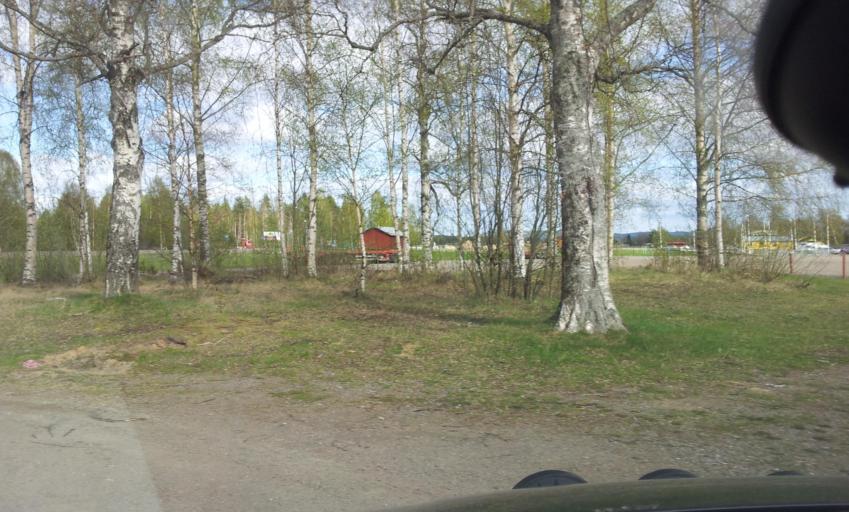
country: SE
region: Gaevleborg
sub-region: Ljusdals Kommun
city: Ljusdal
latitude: 61.8207
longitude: 16.0801
